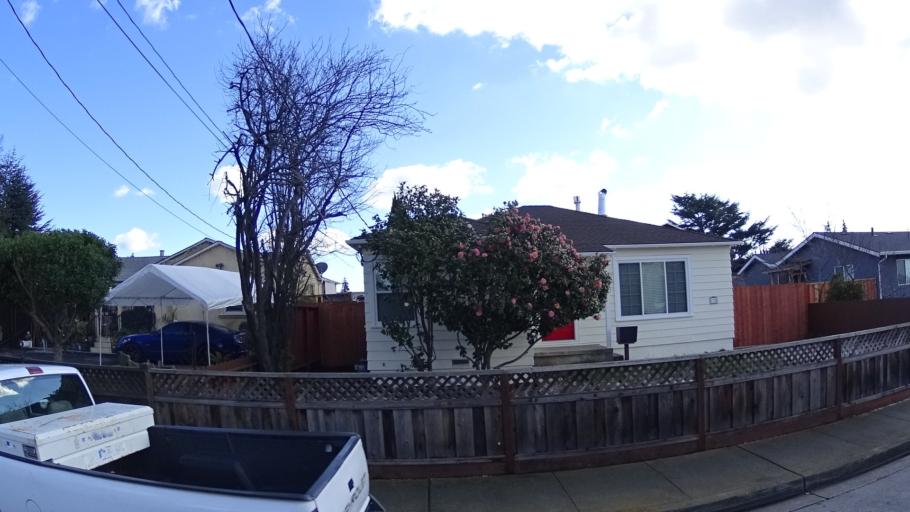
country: US
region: California
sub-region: Alameda County
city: Cherryland
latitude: 37.6781
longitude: -122.1107
